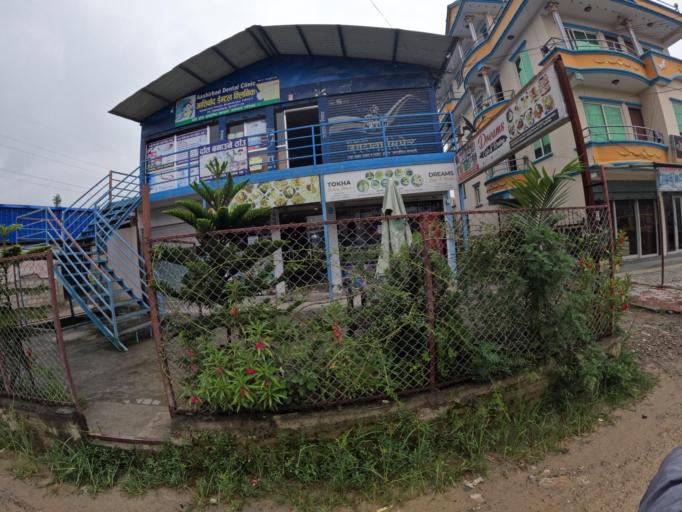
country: NP
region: Central Region
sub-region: Bagmati Zone
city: Kathmandu
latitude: 27.7622
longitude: 85.3189
